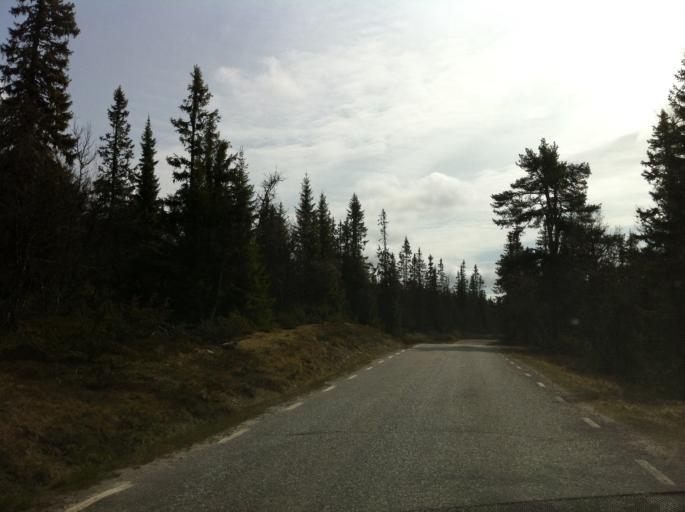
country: NO
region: Hedmark
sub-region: Engerdal
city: Engerdal
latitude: 62.3021
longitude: 12.8013
